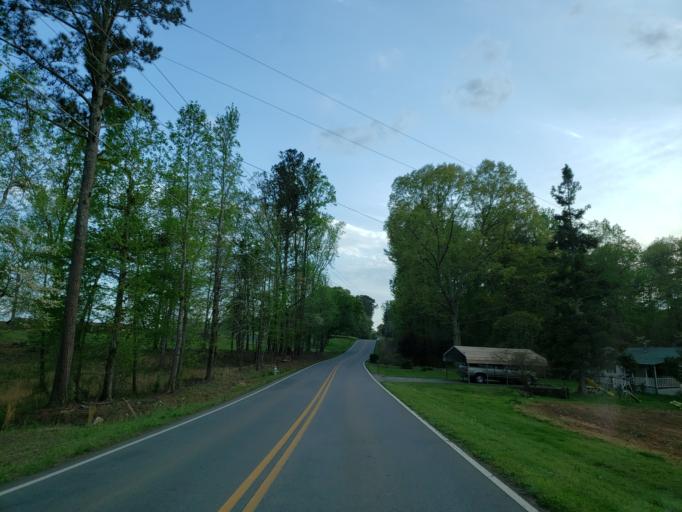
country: US
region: Georgia
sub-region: Cherokee County
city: Canton
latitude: 34.2972
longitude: -84.4489
